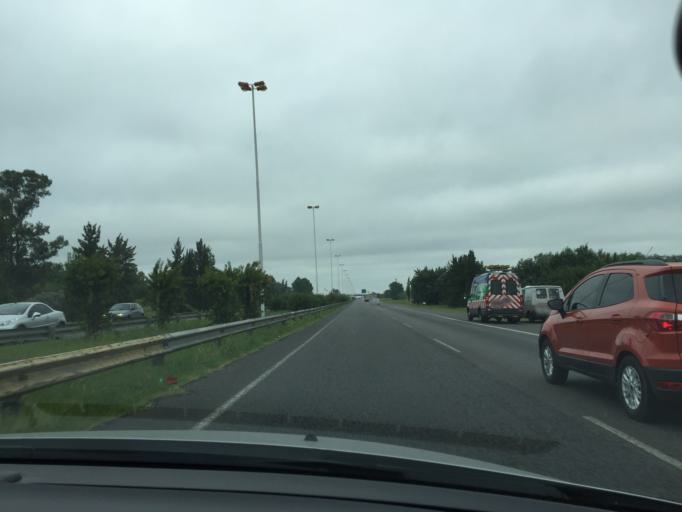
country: AR
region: Buenos Aires
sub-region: Partido de Ezeiza
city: Ezeiza
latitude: -34.8700
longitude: -58.5794
